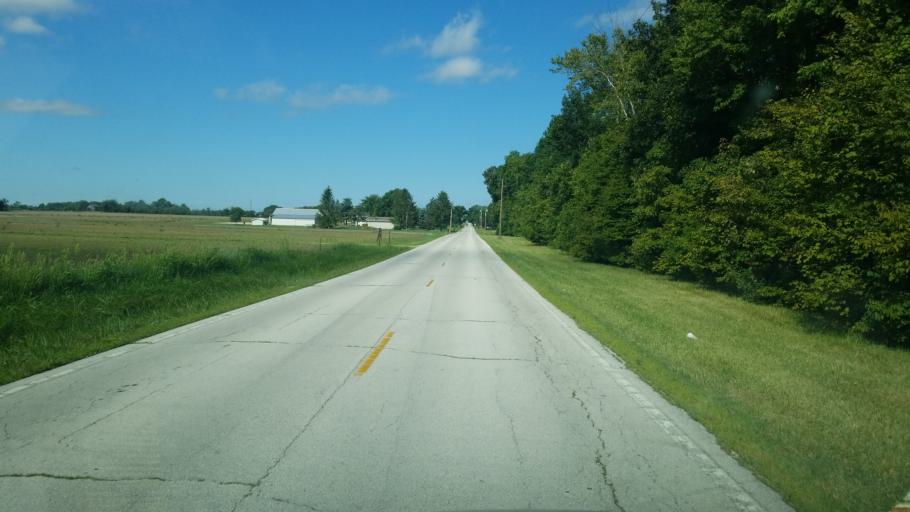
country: US
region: Ohio
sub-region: Seneca County
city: Fostoria
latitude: 41.1083
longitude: -83.4989
